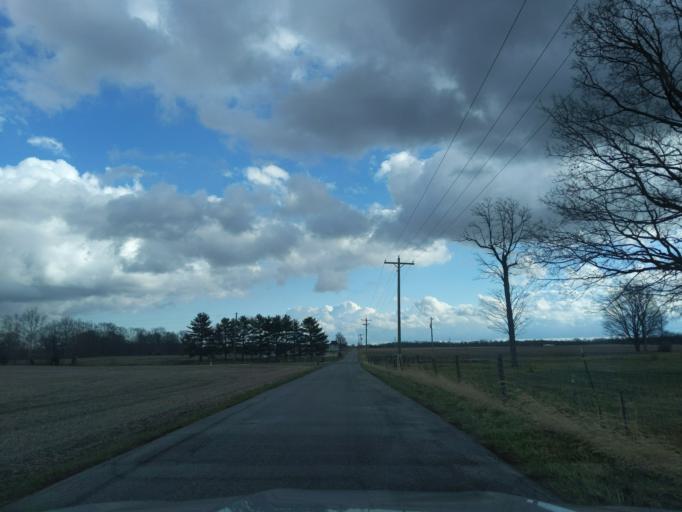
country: US
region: Indiana
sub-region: Decatur County
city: Saint Paul
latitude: 39.4092
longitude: -85.5467
